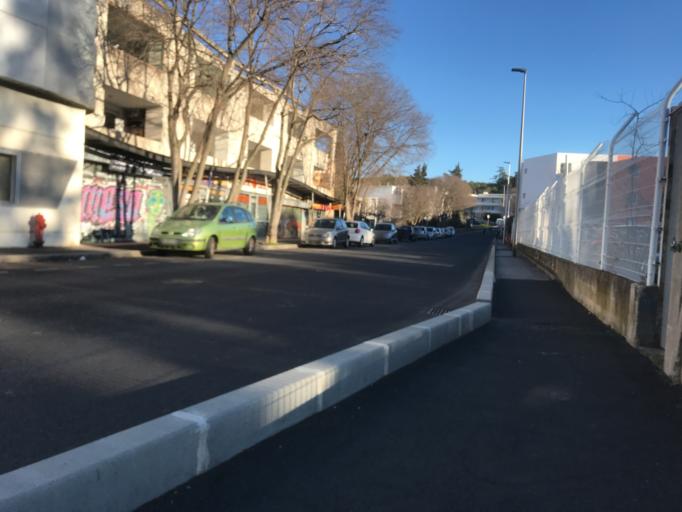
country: FR
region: Languedoc-Roussillon
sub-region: Departement de l'Herault
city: Montpellier
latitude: 43.6365
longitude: 3.8688
